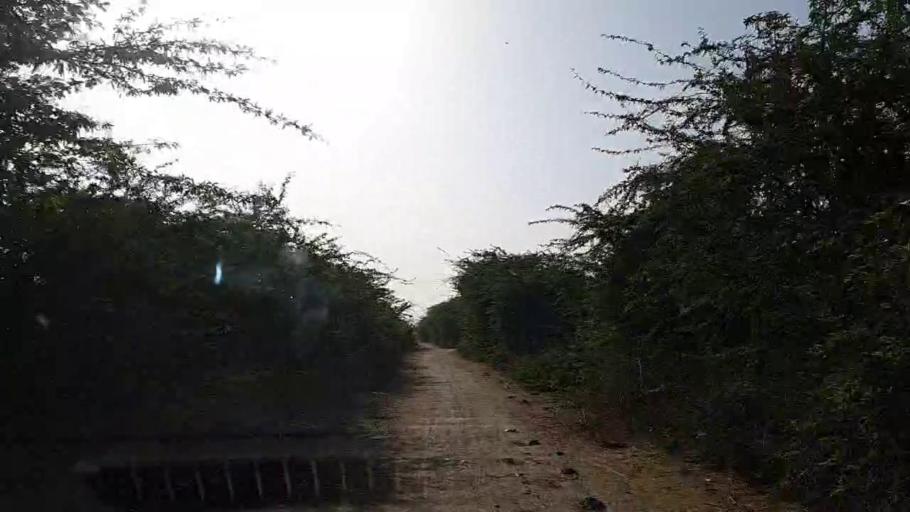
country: PK
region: Sindh
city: Jati
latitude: 24.2848
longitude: 68.1499
